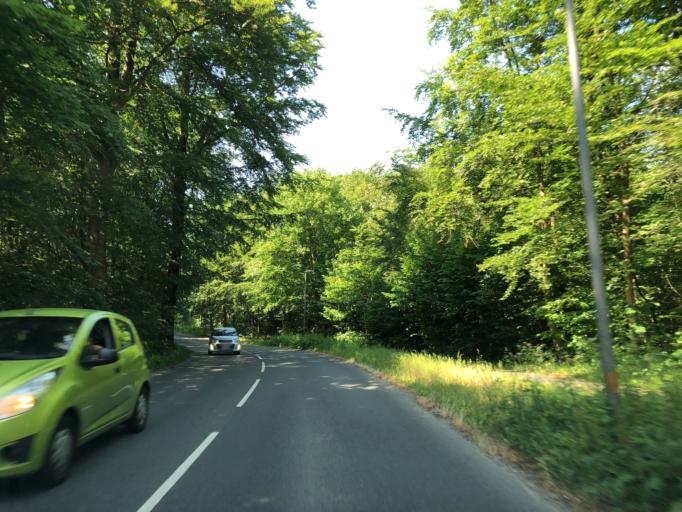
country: DK
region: South Denmark
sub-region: Kolding Kommune
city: Kolding
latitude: 55.5137
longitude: 9.4895
